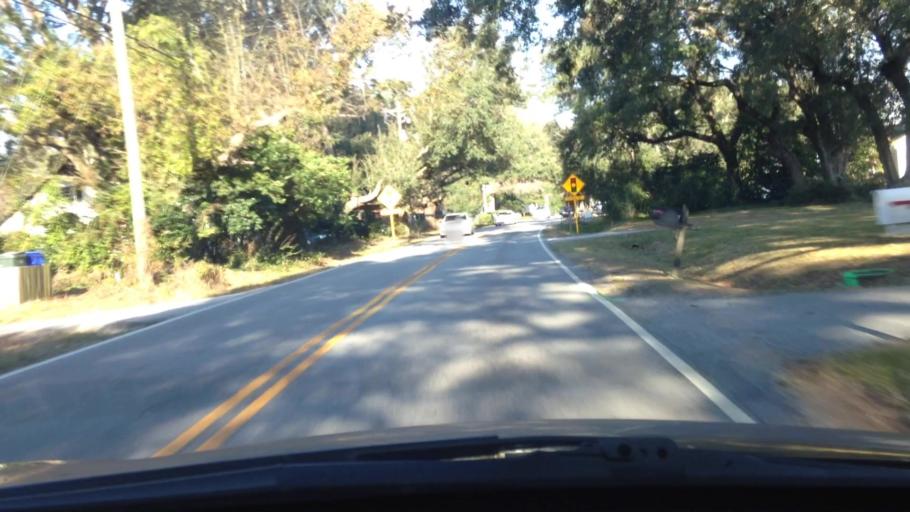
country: US
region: South Carolina
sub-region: Charleston County
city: Charleston
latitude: 32.7540
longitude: -79.9962
